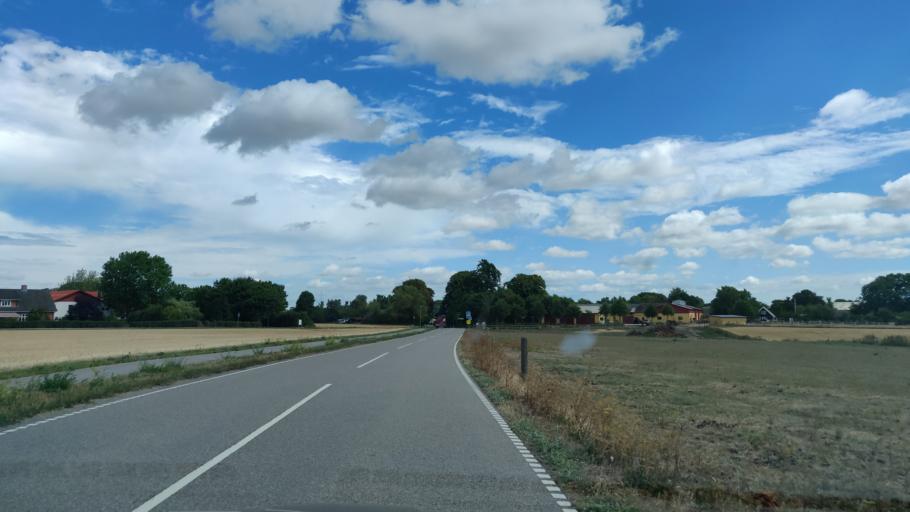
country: DK
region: Capital Region
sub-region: Hoje-Taastrup Kommune
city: Flong
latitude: 55.6626
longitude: 12.1600
